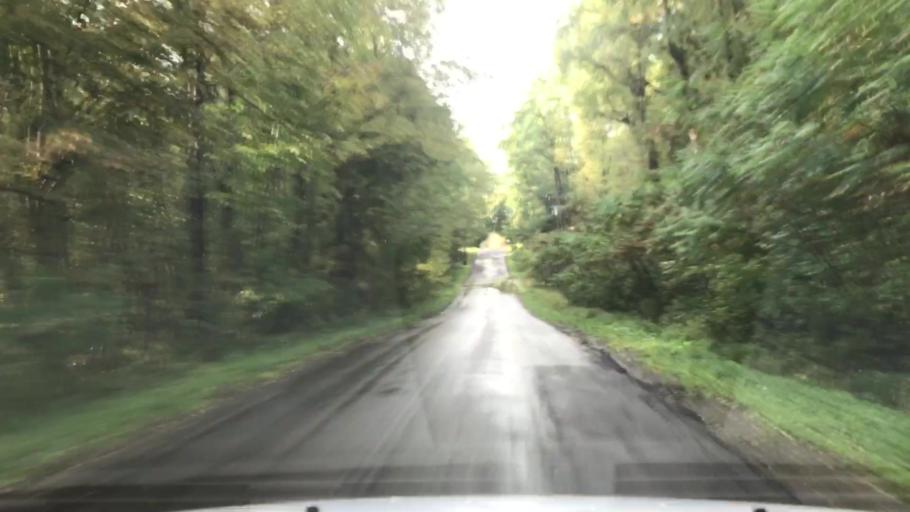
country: US
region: New York
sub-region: Cattaraugus County
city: Little Valley
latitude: 42.3098
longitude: -78.7181
